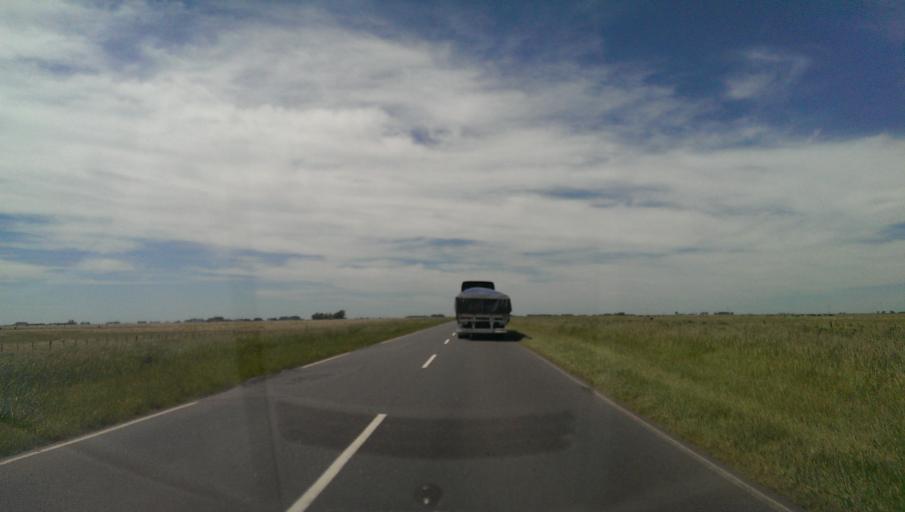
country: AR
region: Buenos Aires
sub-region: Partido de Laprida
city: Laprida
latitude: -37.2419
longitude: -60.7767
